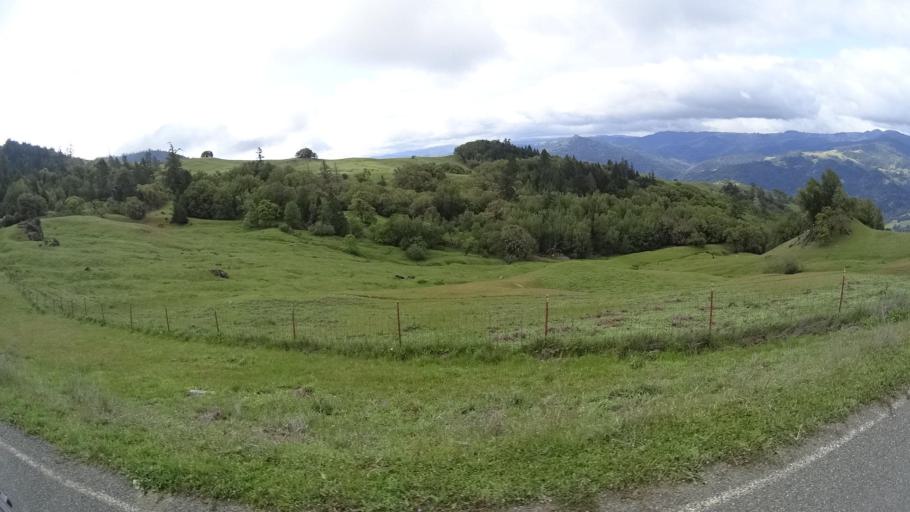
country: US
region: California
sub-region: Humboldt County
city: Redway
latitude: 40.1616
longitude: -123.5653
